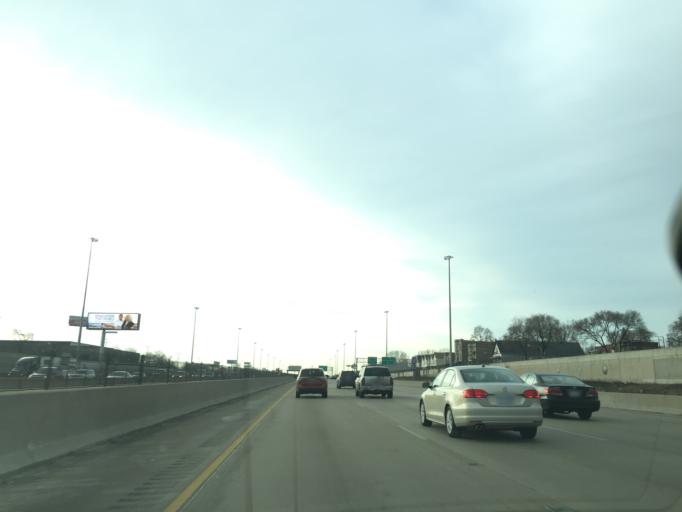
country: US
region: Illinois
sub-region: Cook County
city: Chicago
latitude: 41.8014
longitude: -87.6315
